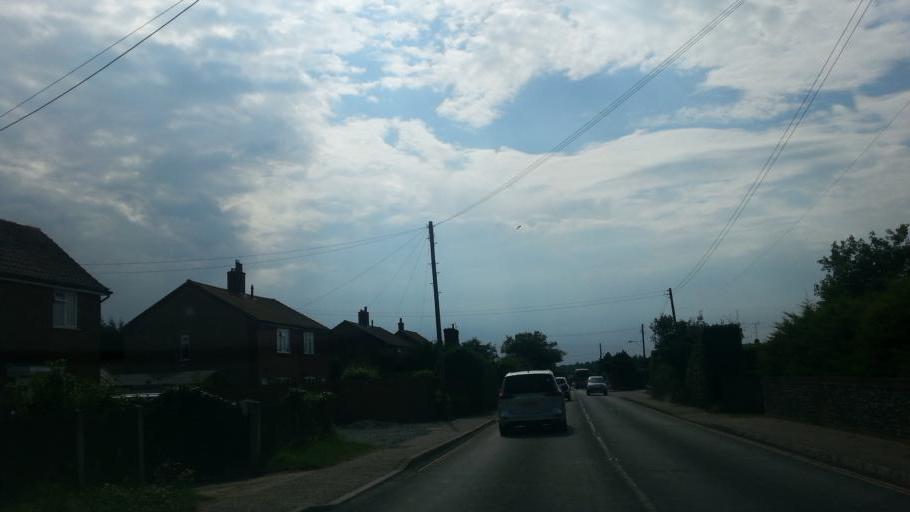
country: GB
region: England
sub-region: Norfolk
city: Sheringham
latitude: 52.9165
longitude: 1.1596
